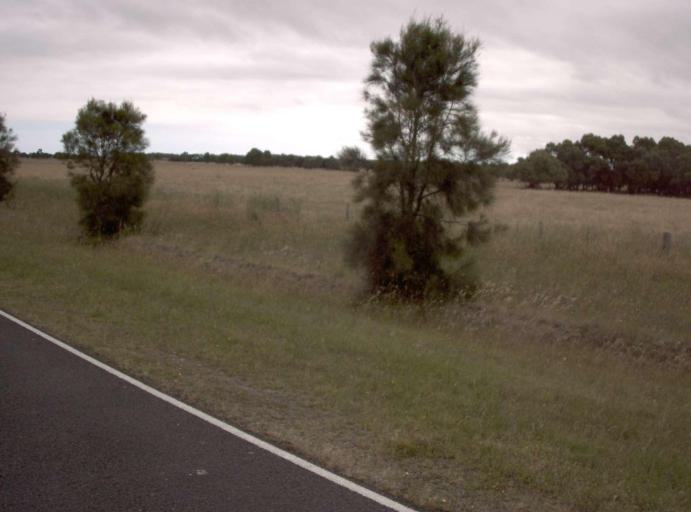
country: AU
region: Victoria
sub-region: Wellington
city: Sale
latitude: -38.5690
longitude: 146.8786
